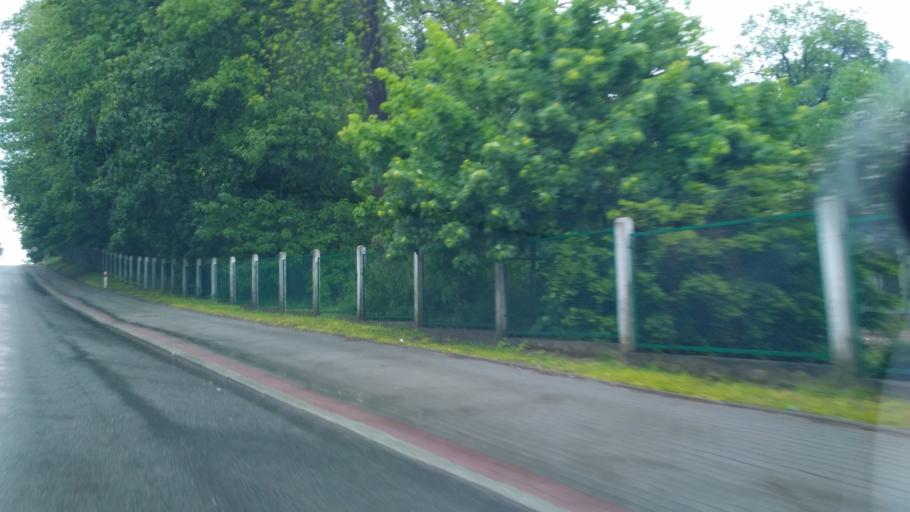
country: PL
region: Subcarpathian Voivodeship
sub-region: Powiat jasielski
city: Jaslo
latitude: 49.7533
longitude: 21.4805
